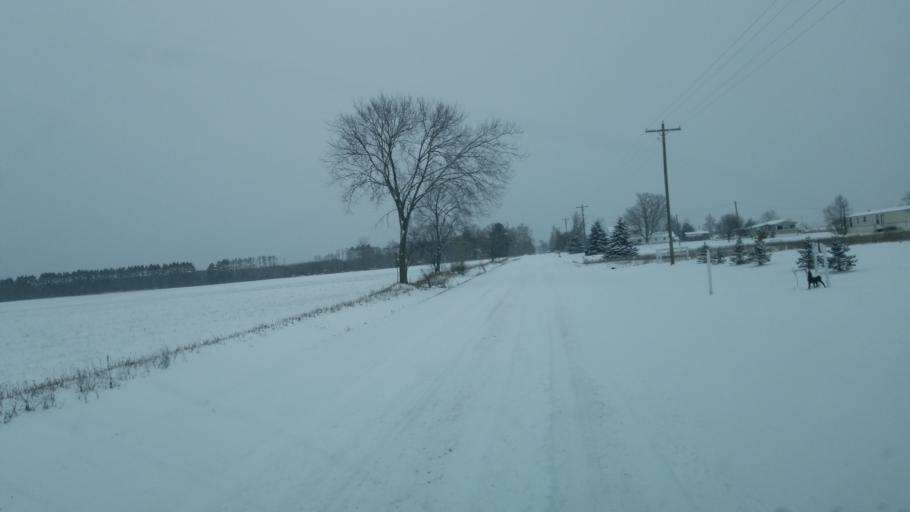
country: US
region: Michigan
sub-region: Osceola County
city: Reed City
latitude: 43.8247
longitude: -85.4140
